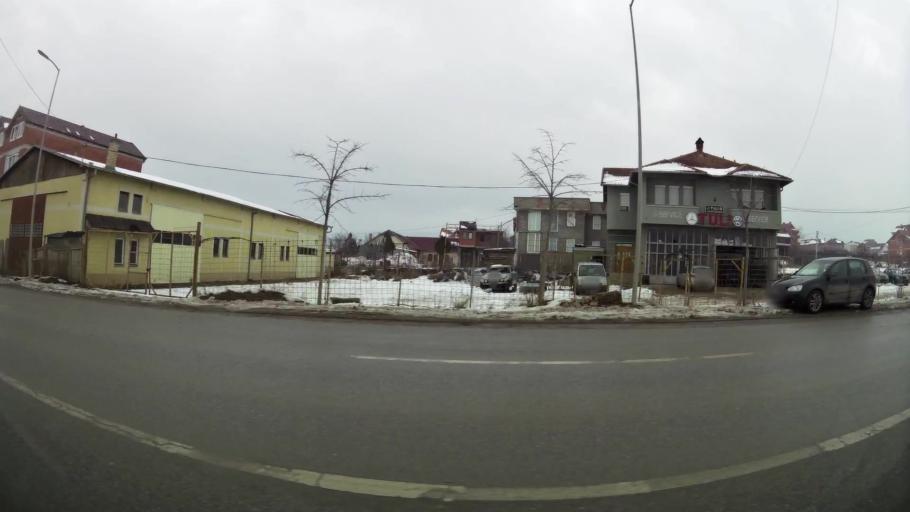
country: XK
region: Pristina
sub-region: Komuna e Prishtines
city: Pristina
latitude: 42.7004
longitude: 21.1589
